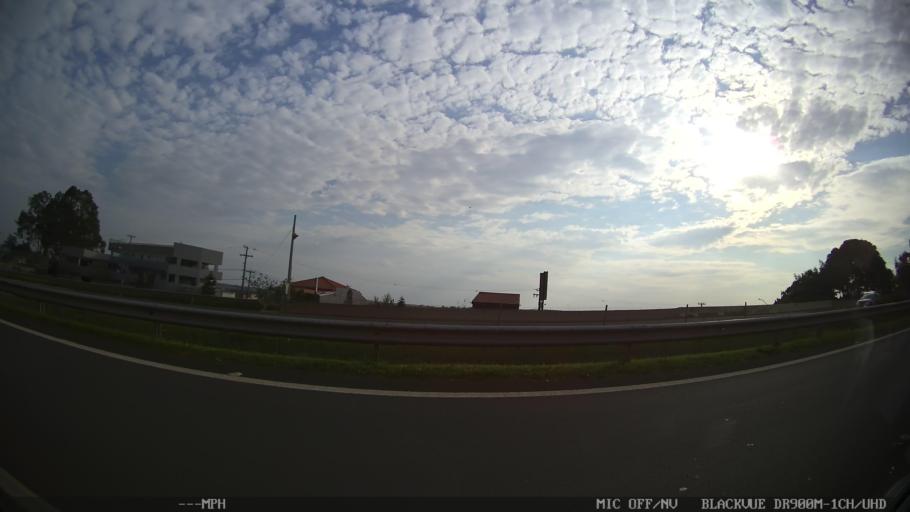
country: BR
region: Sao Paulo
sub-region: Cosmopolis
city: Cosmopolis
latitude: -22.6422
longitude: -47.2091
